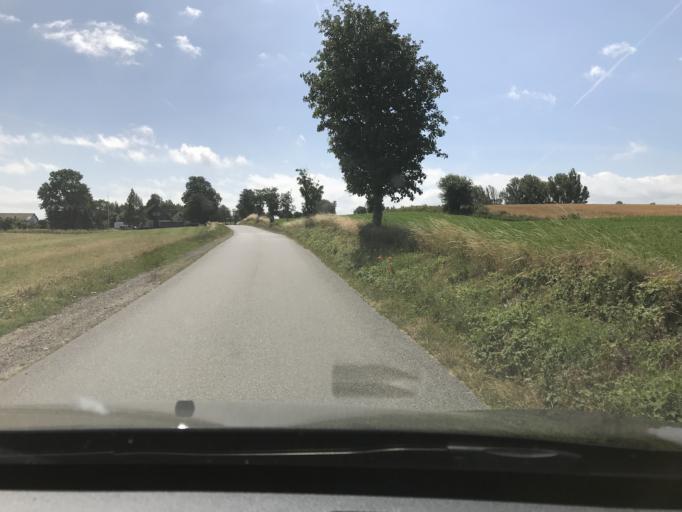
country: DK
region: South Denmark
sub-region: AEro Kommune
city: AEroskobing
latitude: 54.9094
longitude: 10.3014
